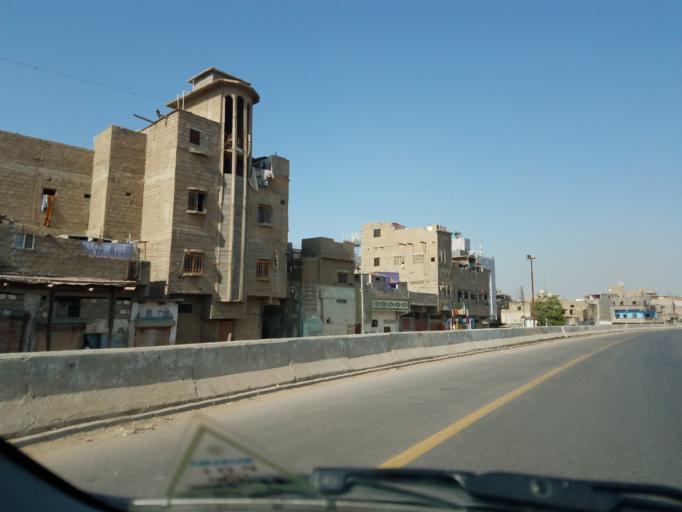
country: PK
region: Sindh
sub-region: Karachi District
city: Karachi
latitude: 24.8885
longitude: 67.0251
